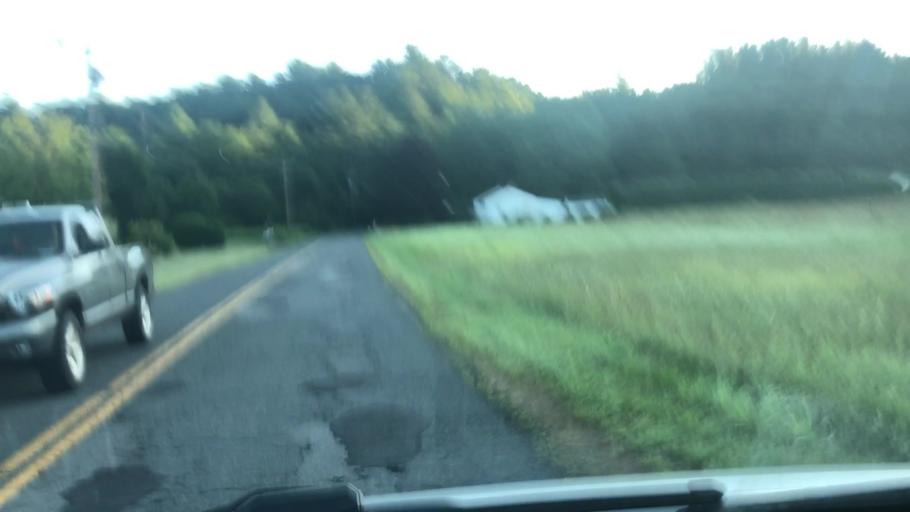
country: US
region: Massachusetts
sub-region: Hampshire County
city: Easthampton
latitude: 42.2785
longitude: -72.7162
